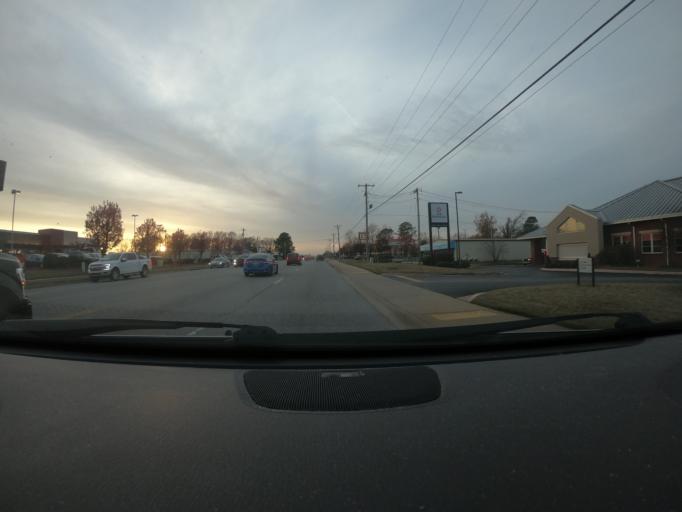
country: US
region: Arkansas
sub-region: Benton County
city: Bentonville
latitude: 36.3353
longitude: -94.1930
